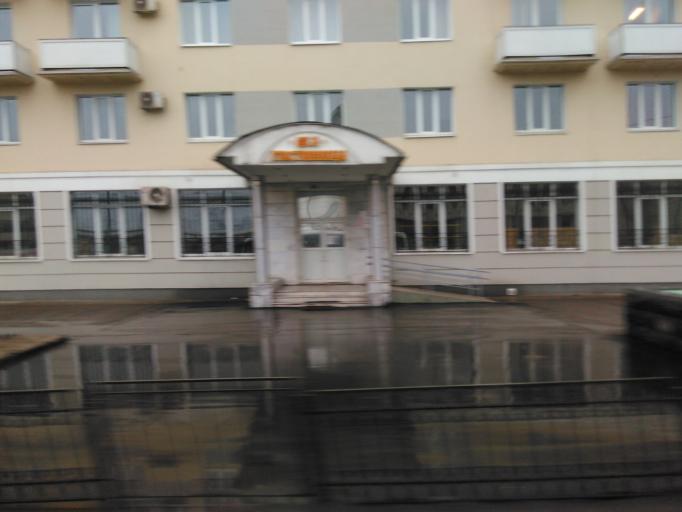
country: RU
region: Tatarstan
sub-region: Gorod Kazan'
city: Kazan
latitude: 55.7903
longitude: 49.1008
